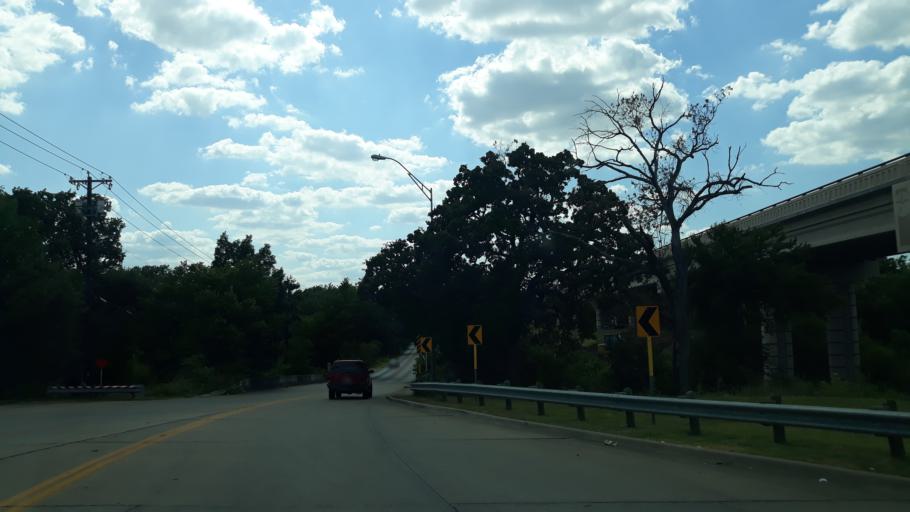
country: US
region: Texas
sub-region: Dallas County
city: Irving
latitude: 32.8156
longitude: -96.9942
